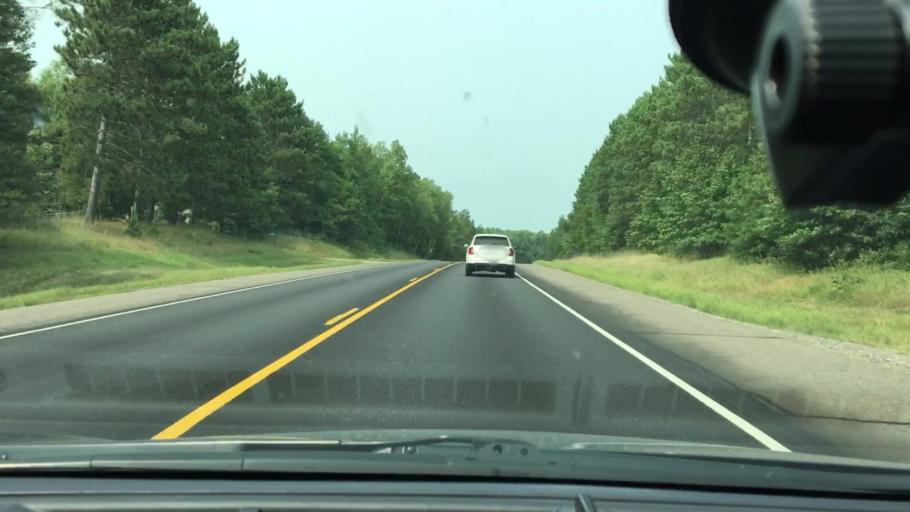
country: US
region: Minnesota
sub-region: Crow Wing County
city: Cross Lake
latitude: 46.6218
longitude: -94.1319
